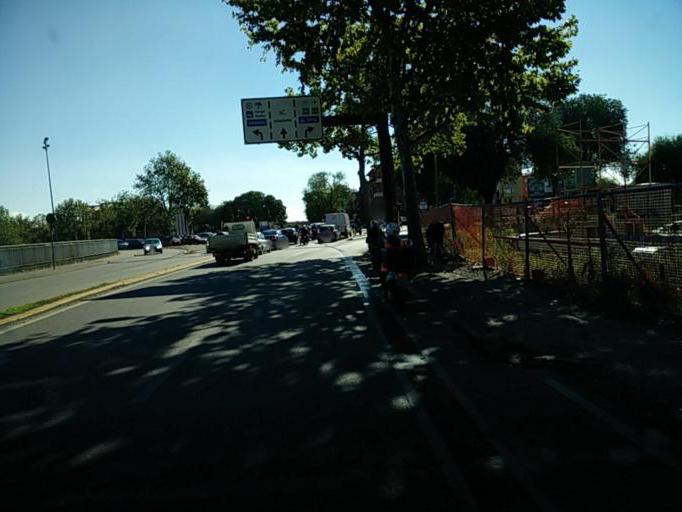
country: IT
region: Veneto
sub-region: Provincia di Verona
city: Verona
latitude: 45.4332
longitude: 10.9797
